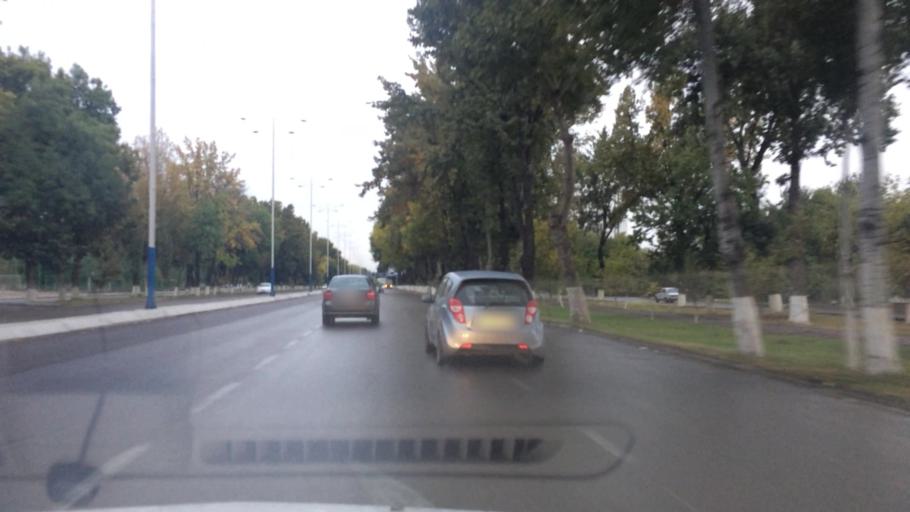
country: UZ
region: Toshkent Shahri
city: Tashkent
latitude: 41.2635
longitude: 69.1982
